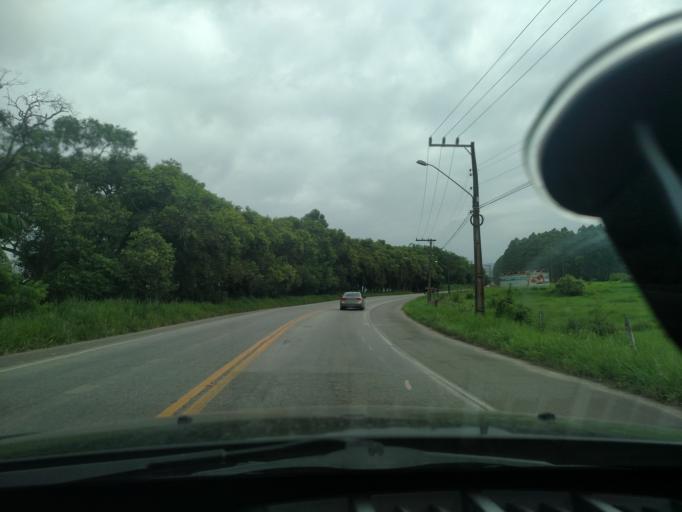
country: BR
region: Santa Catarina
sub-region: Itajai
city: Itajai
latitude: -26.8903
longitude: -48.7747
